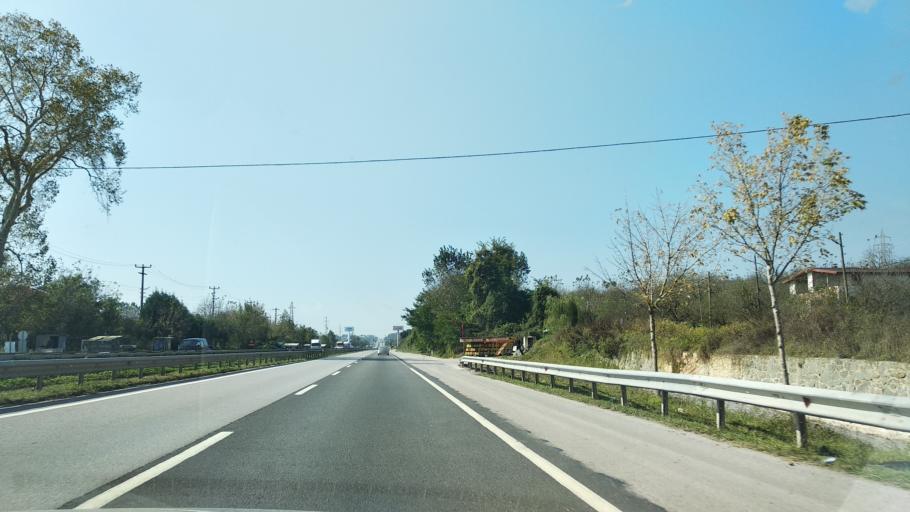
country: TR
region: Sakarya
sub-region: Merkez
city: Sapanca
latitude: 40.7325
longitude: 30.1979
